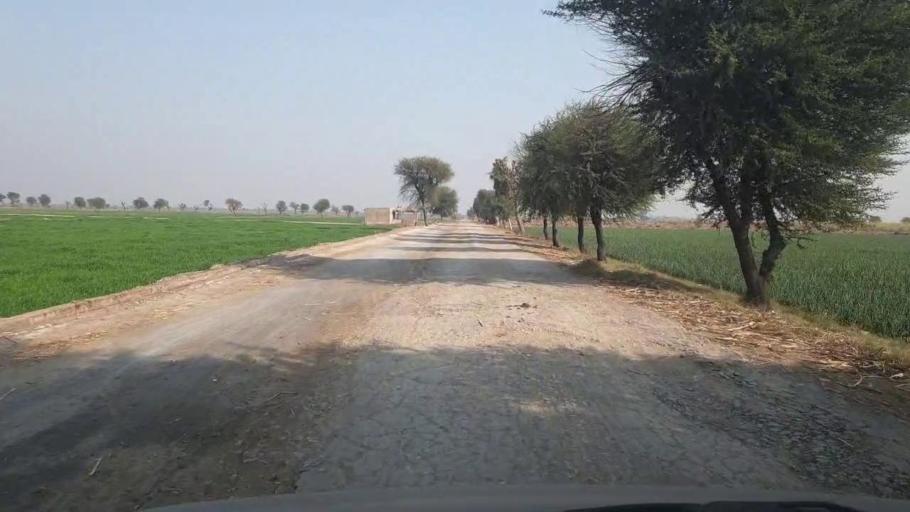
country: PK
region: Sindh
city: Mirwah Gorchani
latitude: 25.2683
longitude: 69.1604
